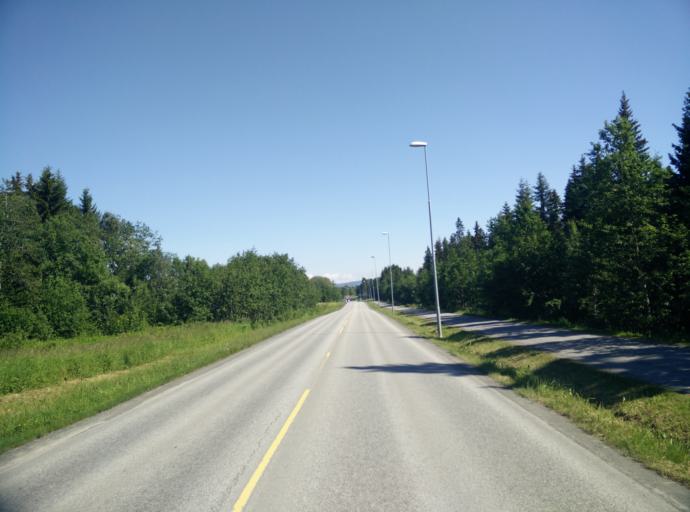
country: NO
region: Sor-Trondelag
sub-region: Trondheim
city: Trondheim
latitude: 63.3729
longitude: 10.3323
